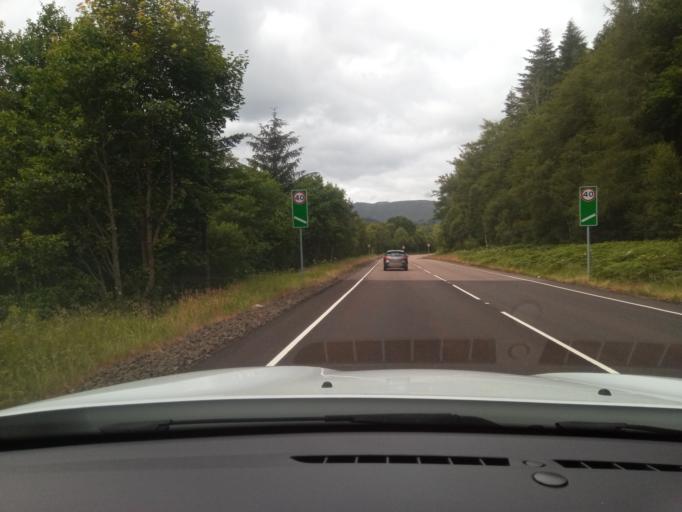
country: GB
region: Scotland
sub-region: Stirling
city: Callander
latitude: 56.3148
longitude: -4.3288
